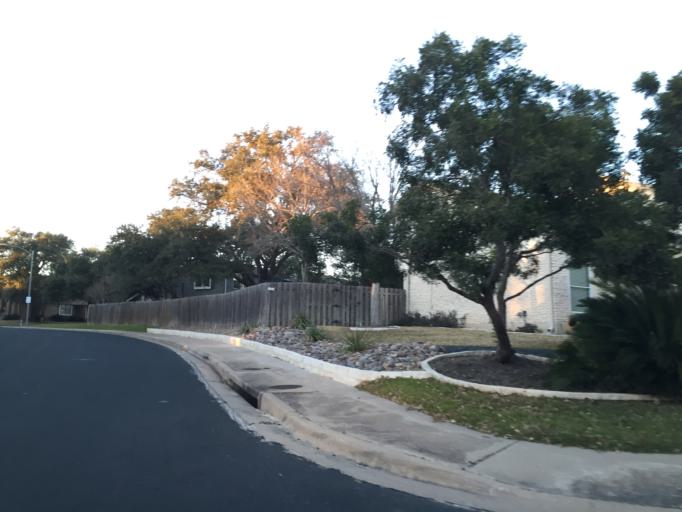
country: US
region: Texas
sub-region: Williamson County
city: Jollyville
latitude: 30.4158
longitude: -97.7619
